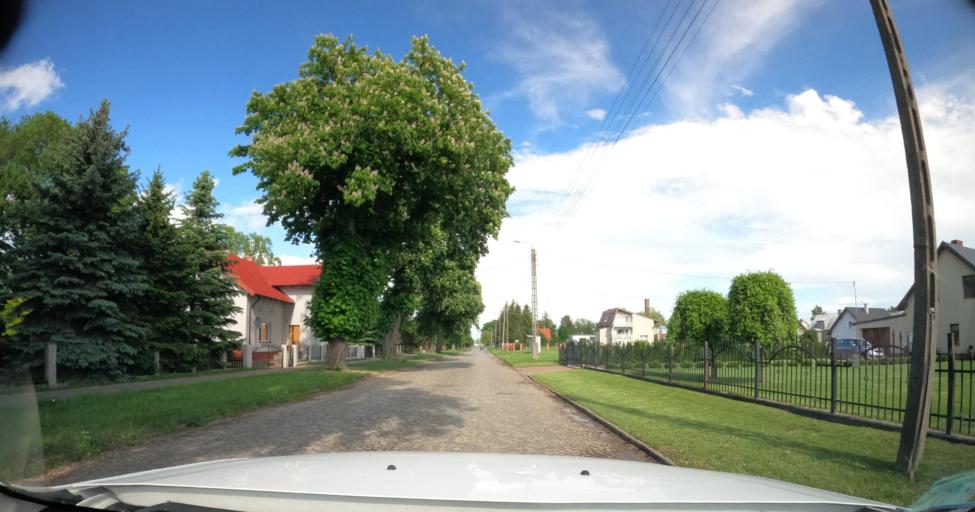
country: PL
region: Pomeranian Voivodeship
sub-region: Powiat nowodworski
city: Nowy Dwor Gdanski
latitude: 54.1888
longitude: 19.1520
